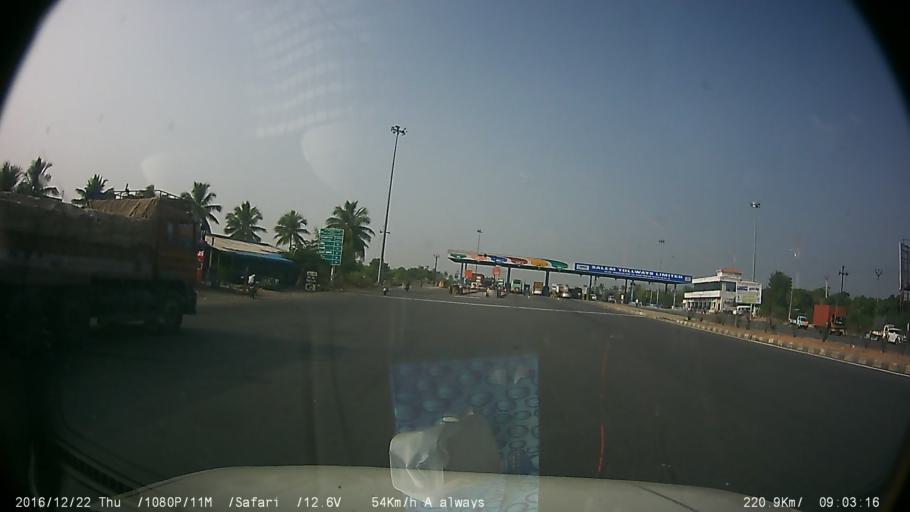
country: IN
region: Tamil Nadu
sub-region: Salem
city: Konganapuram
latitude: 11.5148
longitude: 77.9247
